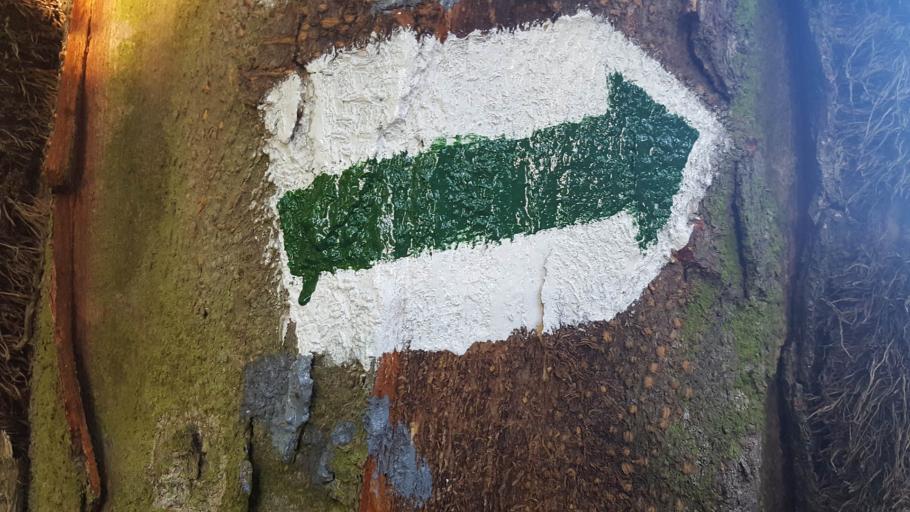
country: HU
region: Somogy
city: Tab
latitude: 46.5842
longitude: 17.9689
